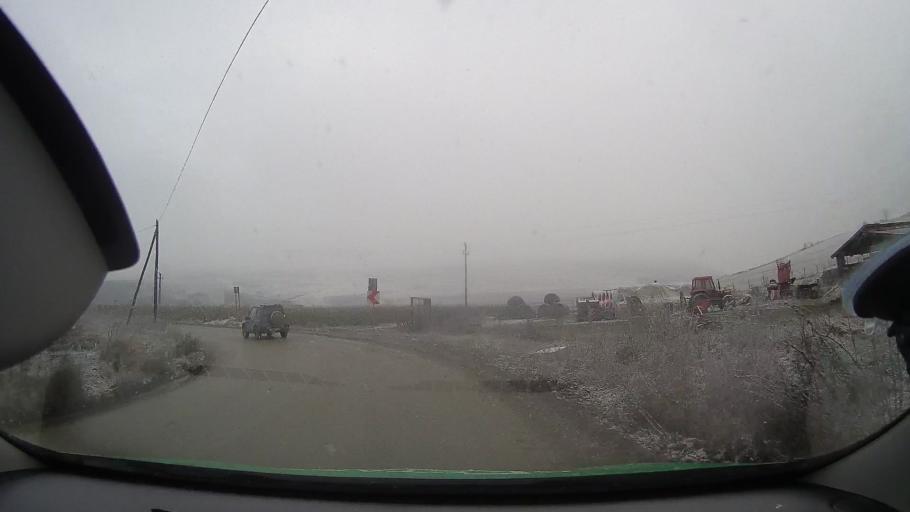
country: RO
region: Alba
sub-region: Comuna Noslac
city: Noslac
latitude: 46.3962
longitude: 23.9125
